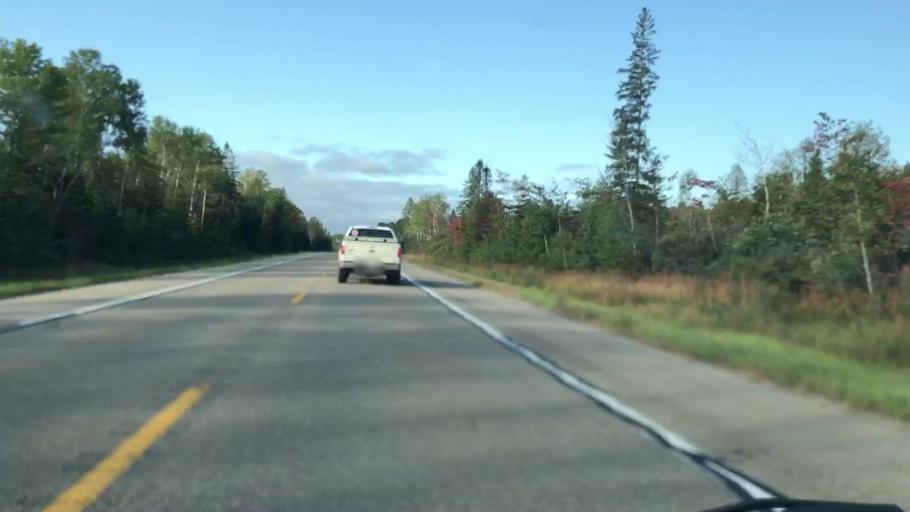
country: US
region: Michigan
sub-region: Luce County
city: Newberry
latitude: 46.3131
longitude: -85.2056
